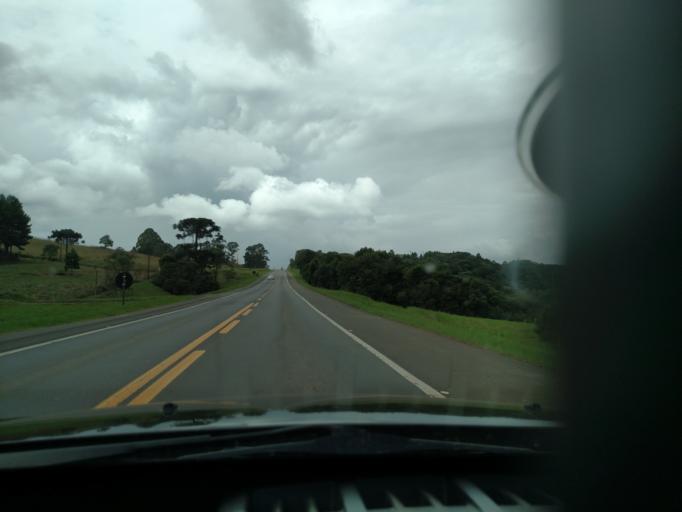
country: BR
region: Santa Catarina
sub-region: Lages
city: Lages
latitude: -27.8250
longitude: -50.3786
